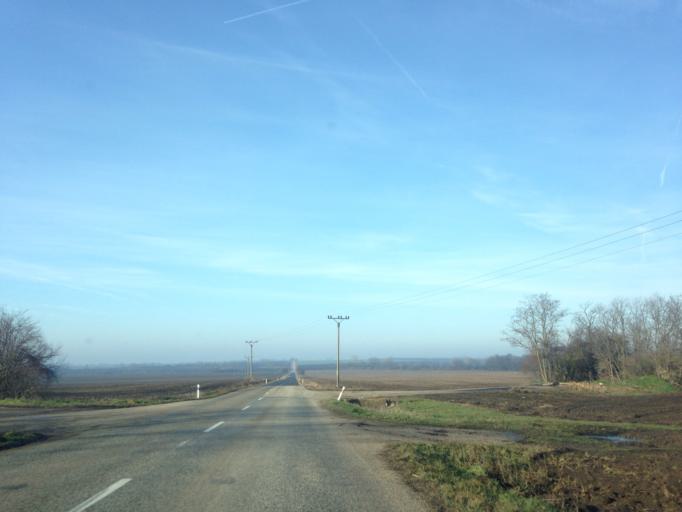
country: SK
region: Nitriansky
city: Svodin
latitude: 47.9836
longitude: 18.3650
